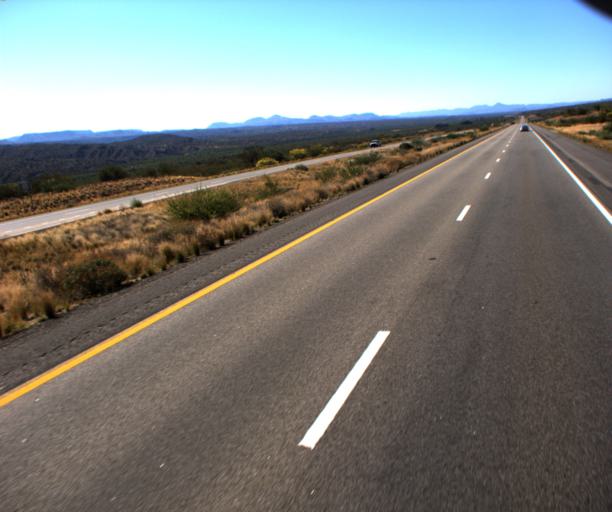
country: US
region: Arizona
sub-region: Mohave County
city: Kingman
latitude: 34.8672
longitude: -113.6438
